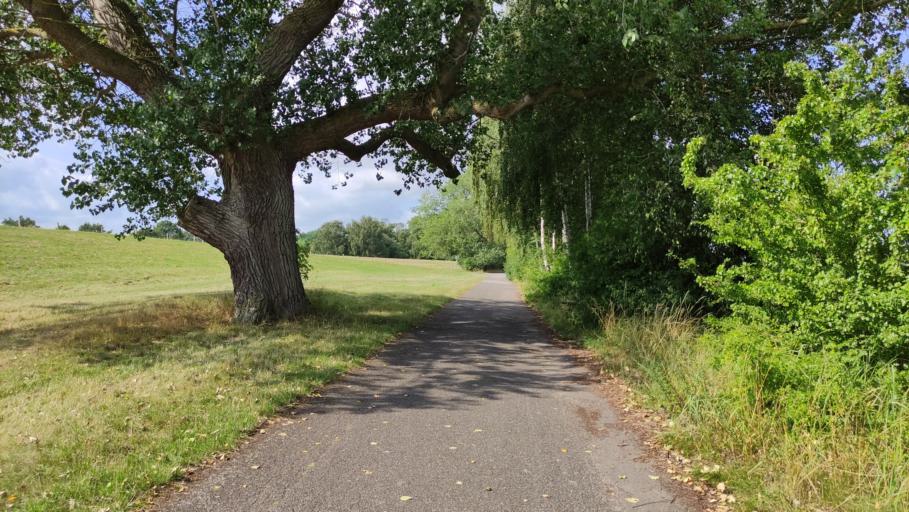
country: DE
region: Schleswig-Holstein
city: Wangels
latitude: 54.3067
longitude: 10.7799
